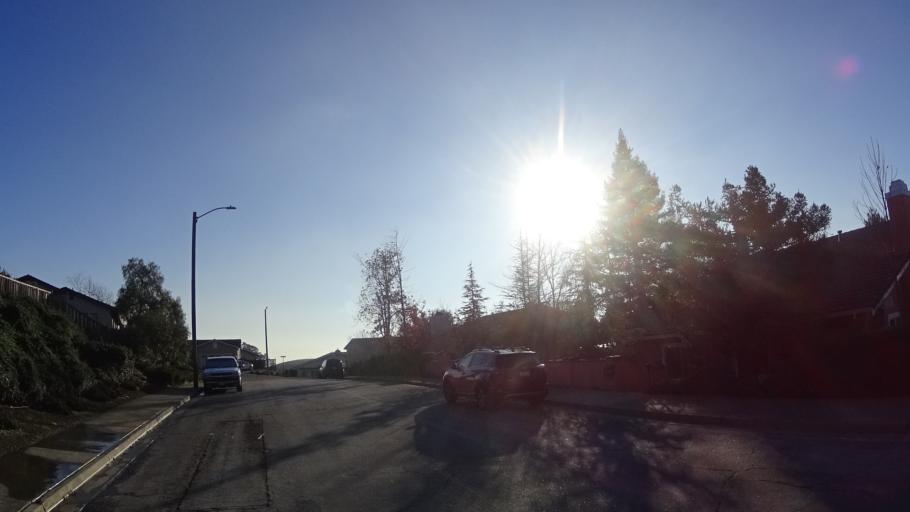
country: US
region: California
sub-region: Alameda County
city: Fairview
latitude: 37.6543
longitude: -122.0420
